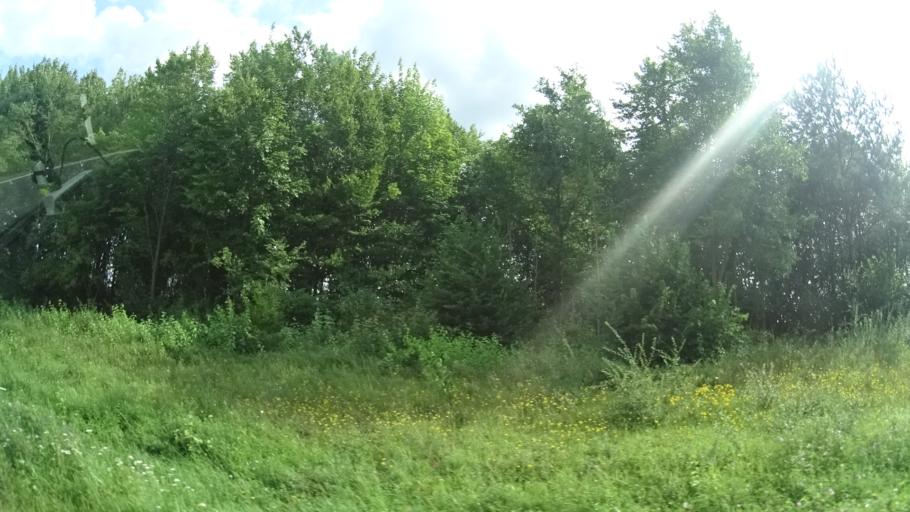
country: DE
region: Bavaria
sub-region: Regierungsbezirk Unterfranken
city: Arnstein
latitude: 49.9700
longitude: 10.0149
